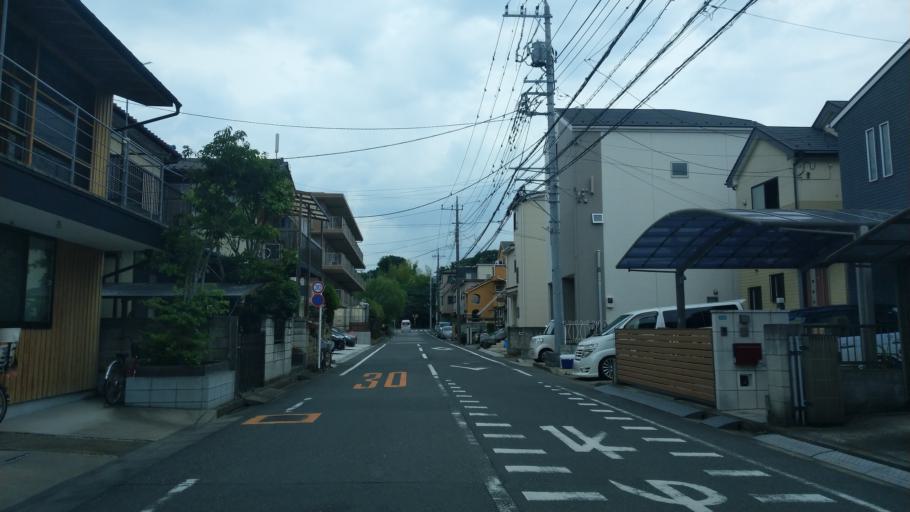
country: JP
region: Saitama
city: Shimotoda
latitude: 35.8566
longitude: 139.6987
